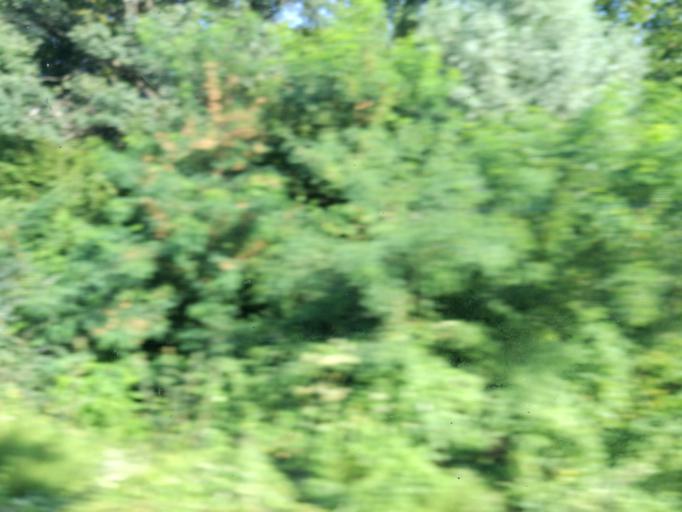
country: RO
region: Iasi
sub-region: Comuna Mogosesti
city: Mogosesti
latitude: 47.0057
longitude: 27.5485
